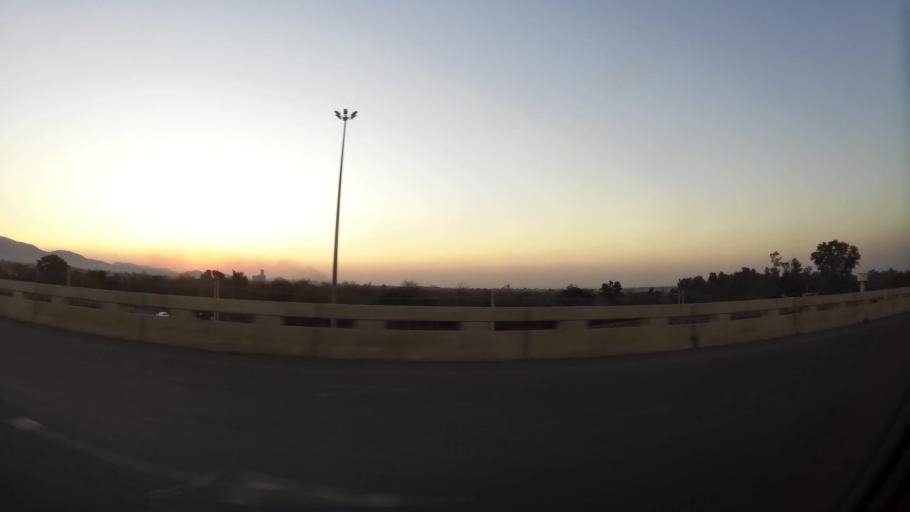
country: ZA
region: North-West
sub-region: Bojanala Platinum District Municipality
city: Rustenburg
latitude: -25.6471
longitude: 27.2558
